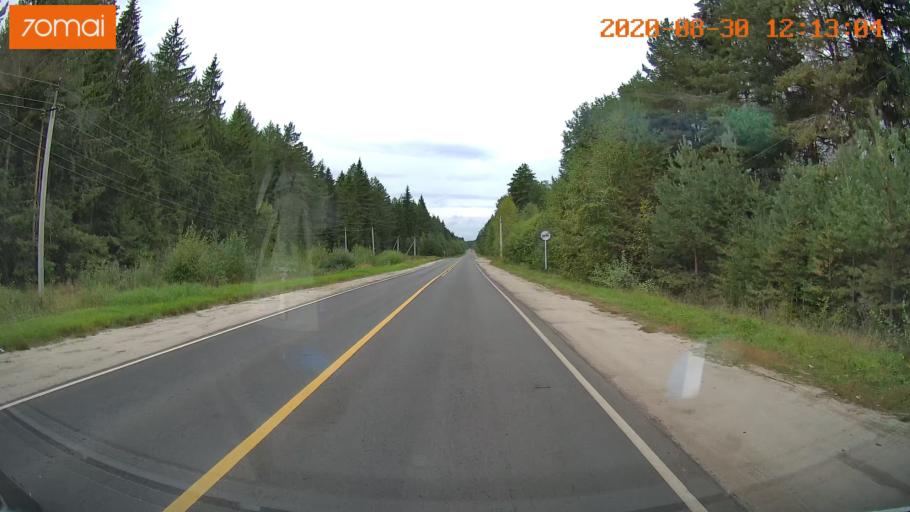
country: RU
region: Ivanovo
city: Yur'yevets
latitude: 57.3121
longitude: 43.0857
